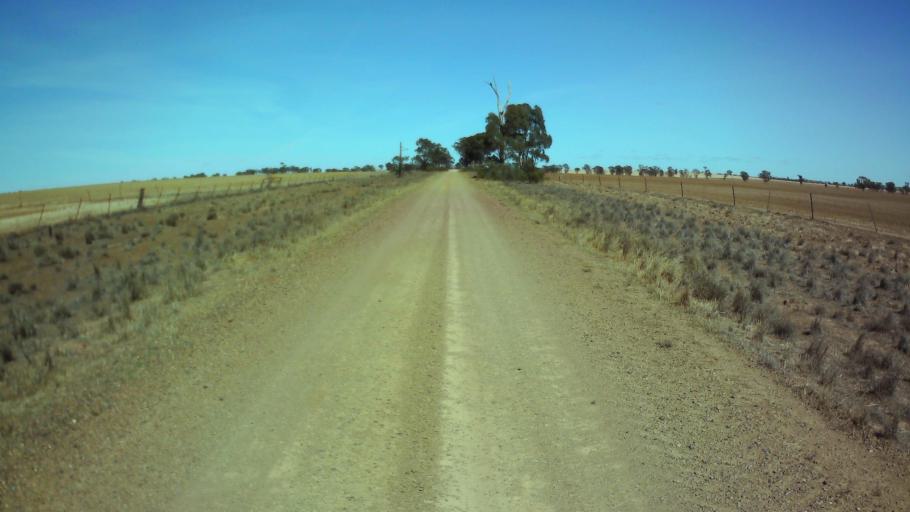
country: AU
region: New South Wales
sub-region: Weddin
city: Grenfell
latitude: -33.7497
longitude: 147.8912
